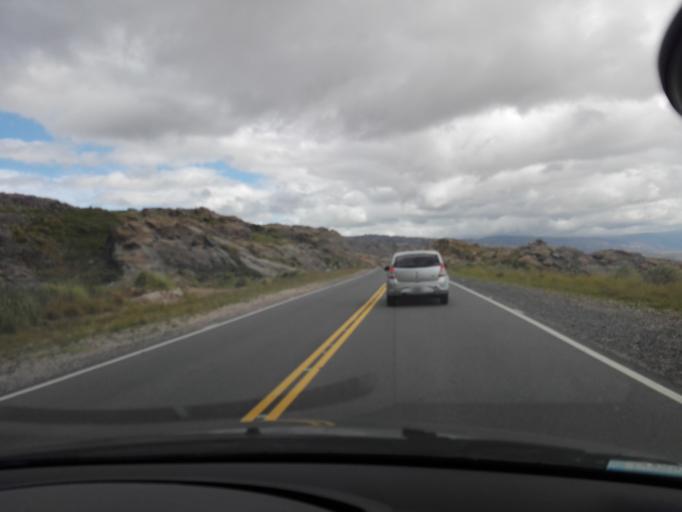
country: AR
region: Cordoba
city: Mina Clavero
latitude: -31.6387
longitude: -64.9073
